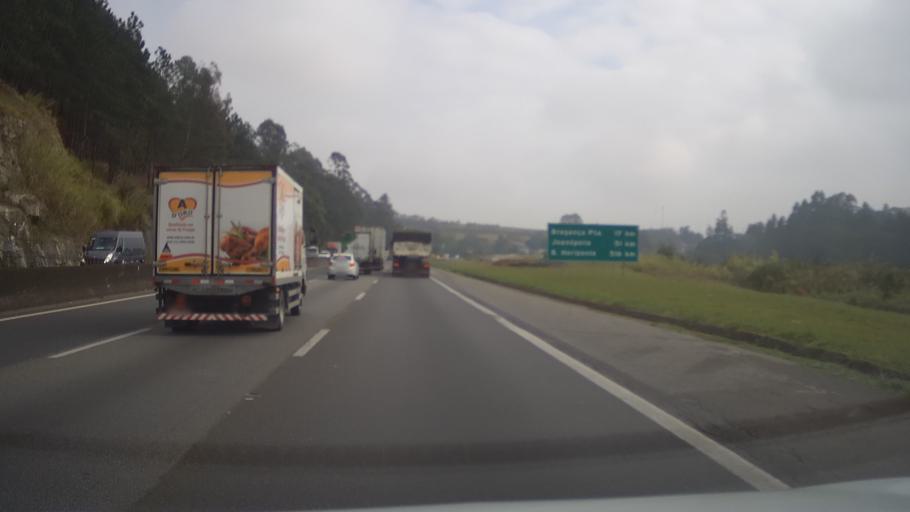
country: BR
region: Sao Paulo
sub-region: Atibaia
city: Atibaia
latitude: -23.0823
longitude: -46.5697
